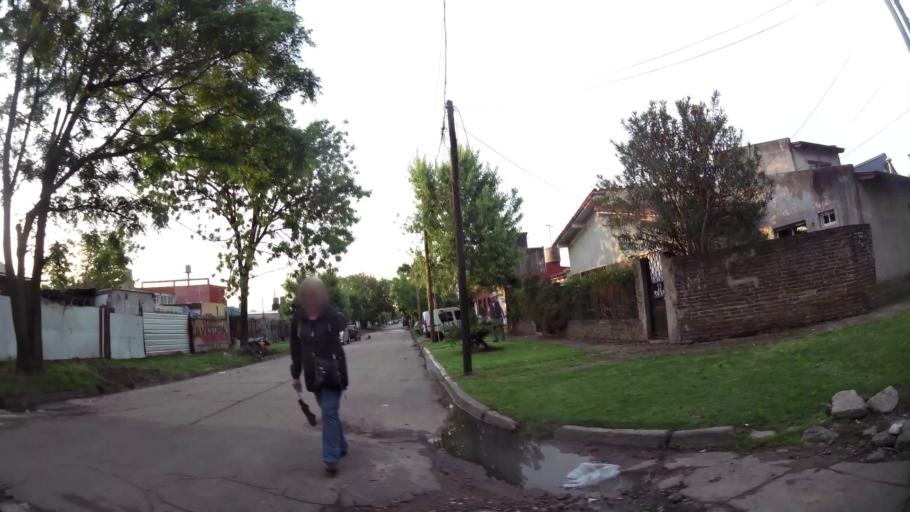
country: AR
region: Buenos Aires
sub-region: Partido de Almirante Brown
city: Adrogue
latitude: -34.7609
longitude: -58.3492
